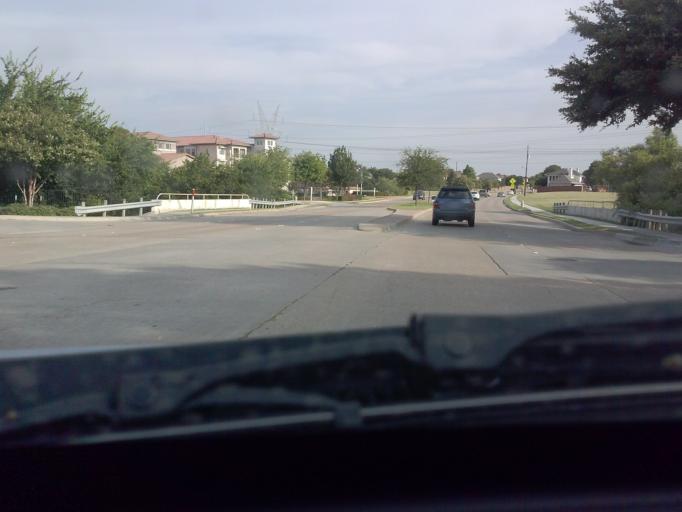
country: US
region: Texas
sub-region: Collin County
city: Frisco
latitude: 33.0591
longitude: -96.7905
